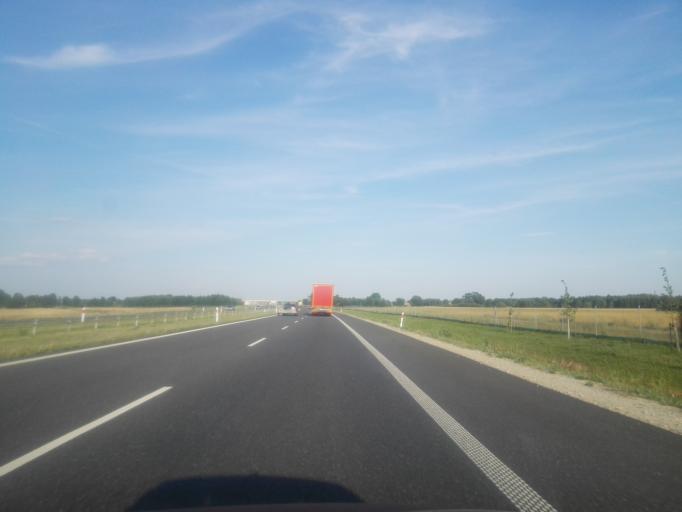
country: PL
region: Lodz Voivodeship
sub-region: Powiat wieruszowski
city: Sokolniki
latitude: 51.3194
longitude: 18.3515
